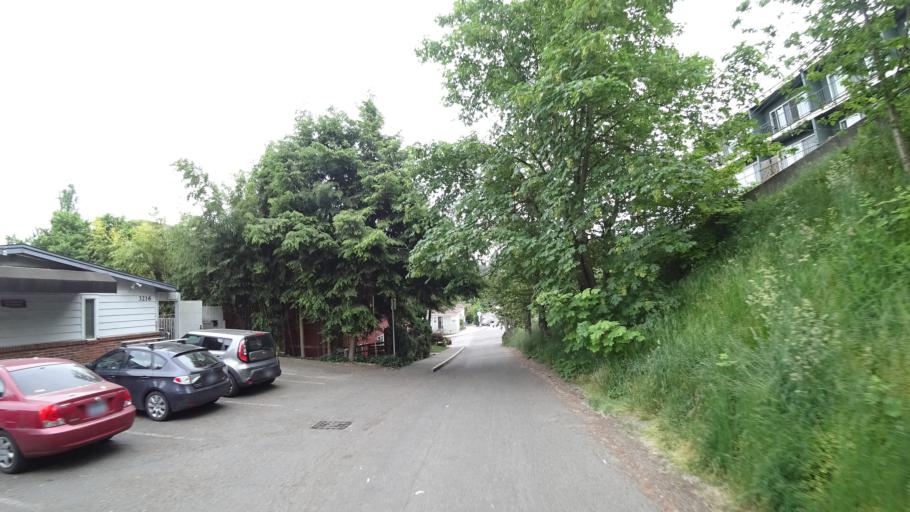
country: US
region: Oregon
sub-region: Multnomah County
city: Portland
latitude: 45.4996
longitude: -122.6912
